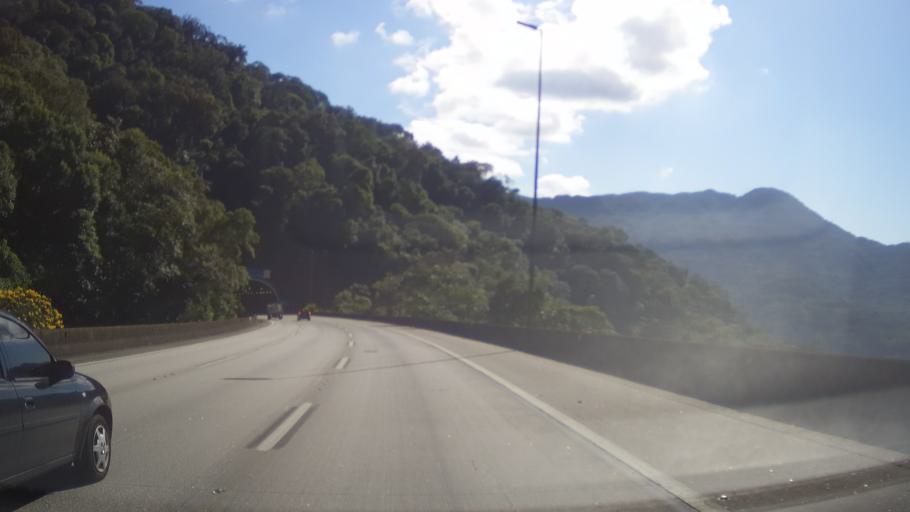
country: BR
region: Sao Paulo
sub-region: Cubatao
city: Cubatao
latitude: -23.8835
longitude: -46.4937
